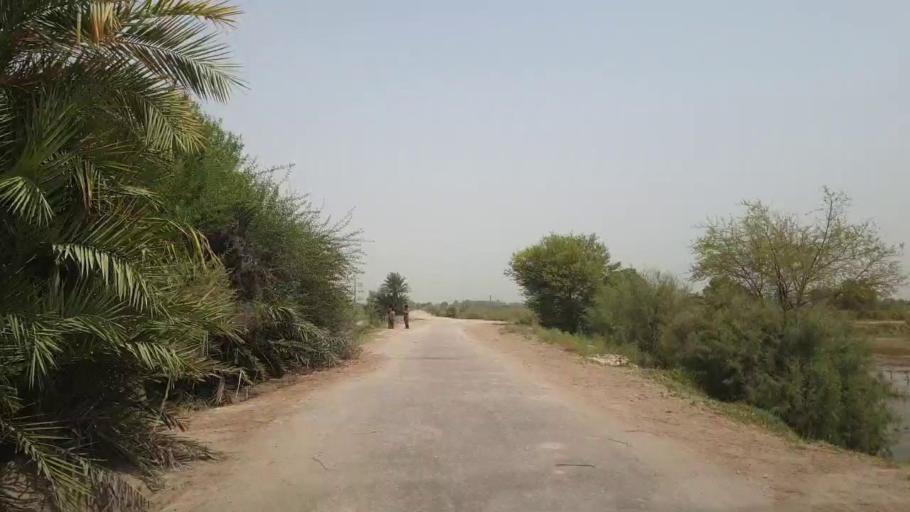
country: PK
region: Sindh
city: Gambat
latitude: 27.4459
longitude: 68.4448
